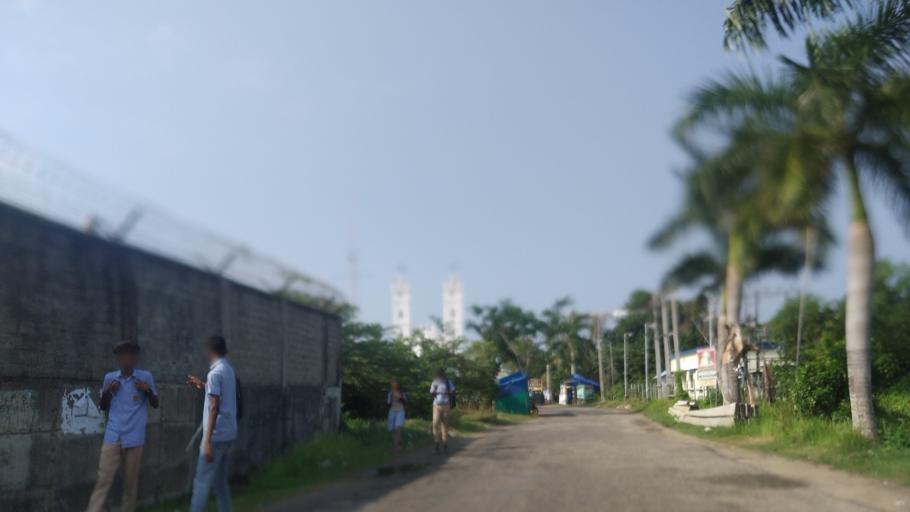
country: IN
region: Kerala
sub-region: Ernakulam
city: Cochin
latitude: 9.9877
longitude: 76.2501
